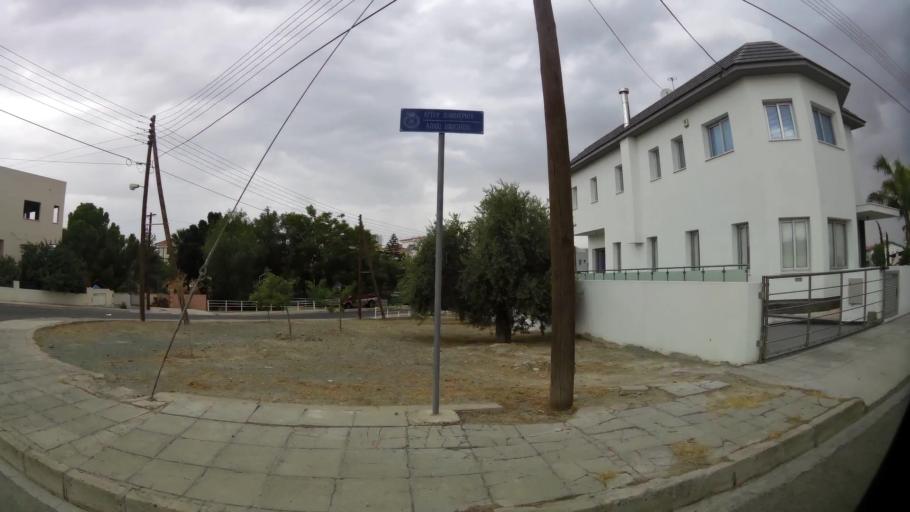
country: CY
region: Lefkosia
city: Geri
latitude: 35.1085
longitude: 33.3876
